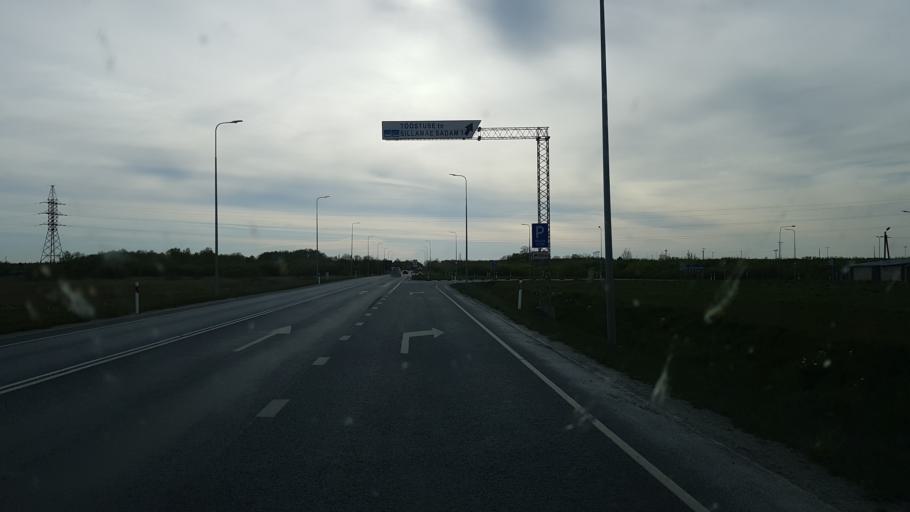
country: EE
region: Ida-Virumaa
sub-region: Sillamaee linn
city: Sillamae
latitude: 59.3909
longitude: 27.7359
